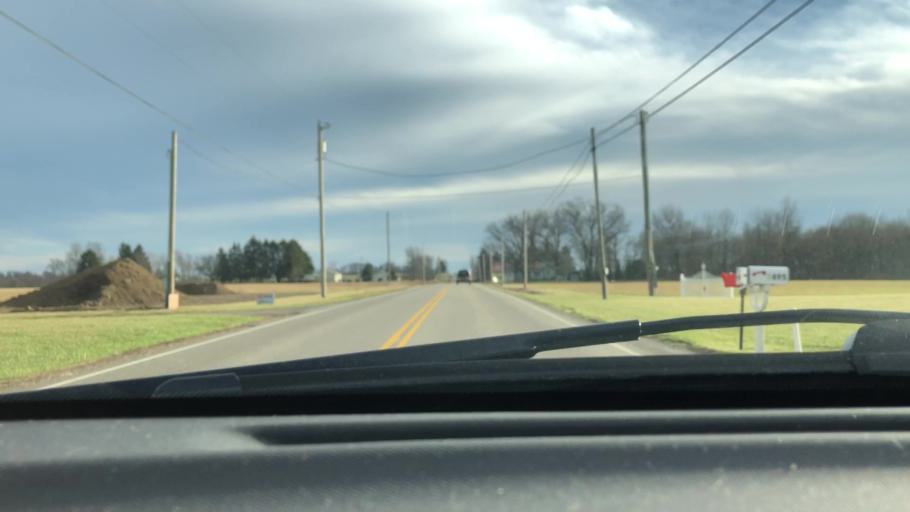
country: US
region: Ohio
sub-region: Wayne County
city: Dalton
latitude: 40.7817
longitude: -81.7453
